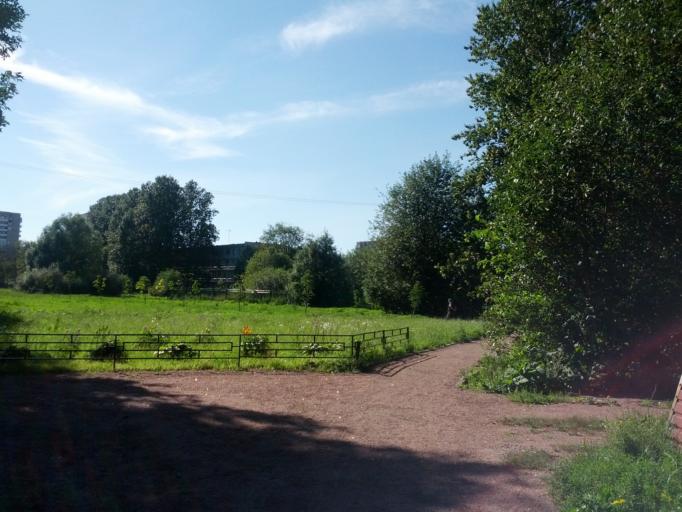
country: RU
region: Leningrad
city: Rybatskoye
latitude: 59.8957
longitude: 30.4868
